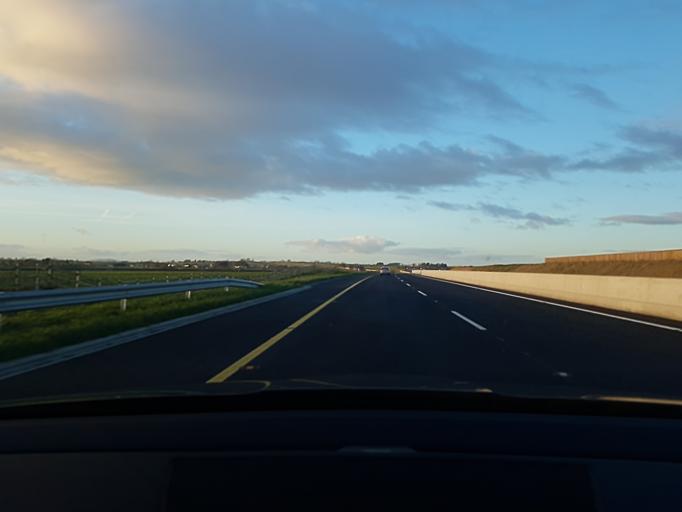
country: IE
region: Connaught
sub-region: County Galway
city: Athenry
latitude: 53.3836
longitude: -8.7998
